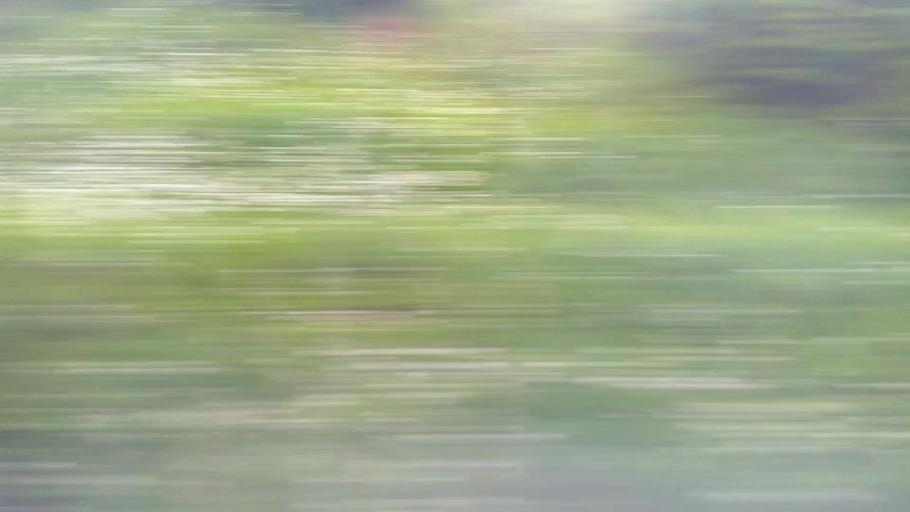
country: RU
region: Moskovskaya
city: Il'inskoye
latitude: 55.1962
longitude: 37.9252
